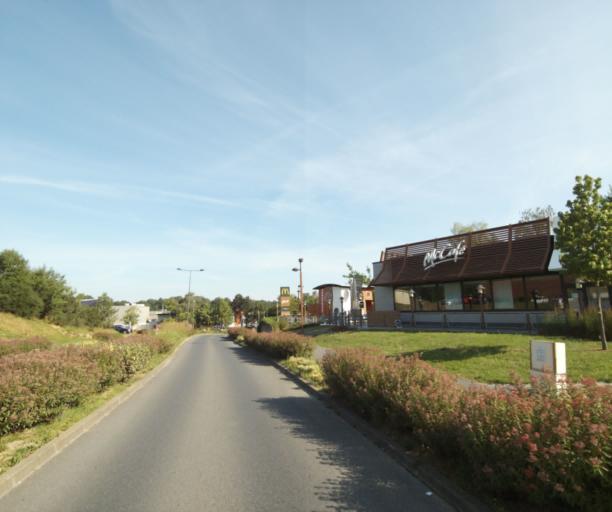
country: FR
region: Champagne-Ardenne
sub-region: Departement des Ardennes
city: La Francheville
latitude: 49.7375
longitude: 4.7077
